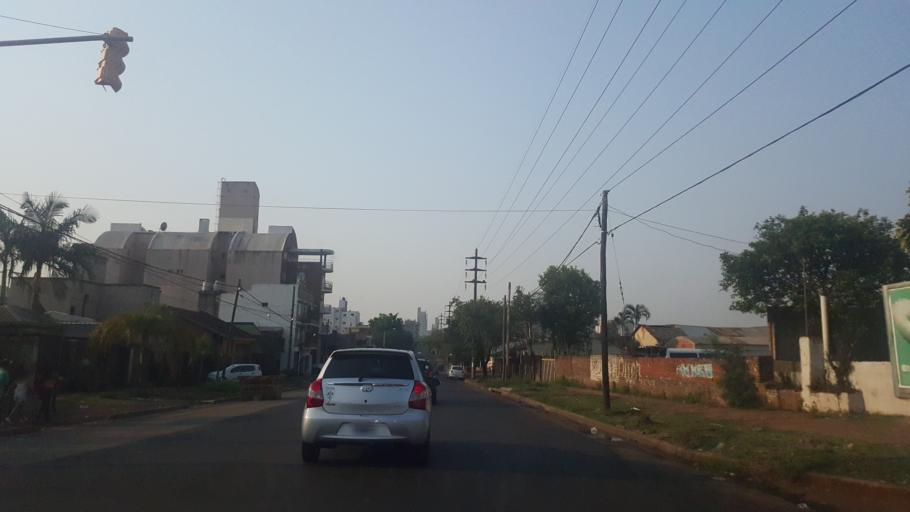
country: AR
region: Misiones
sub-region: Departamento de Capital
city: Posadas
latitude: -27.3818
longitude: -55.8919
